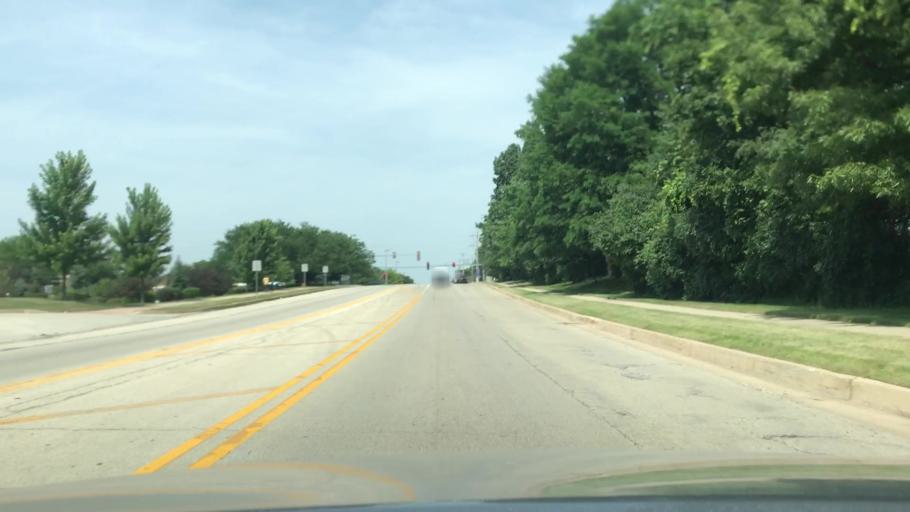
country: US
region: Illinois
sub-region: DuPage County
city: Darien
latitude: 41.7366
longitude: -88.0098
